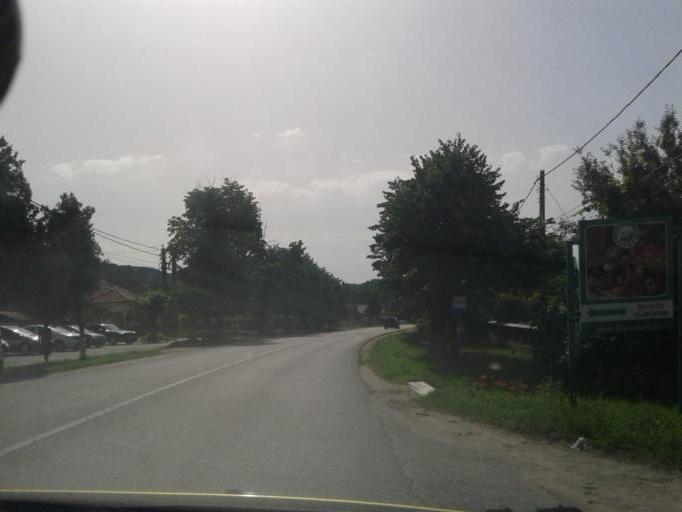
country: RO
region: Valcea
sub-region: Comuna Bunesti
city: Bunesti
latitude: 45.1071
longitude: 24.1984
